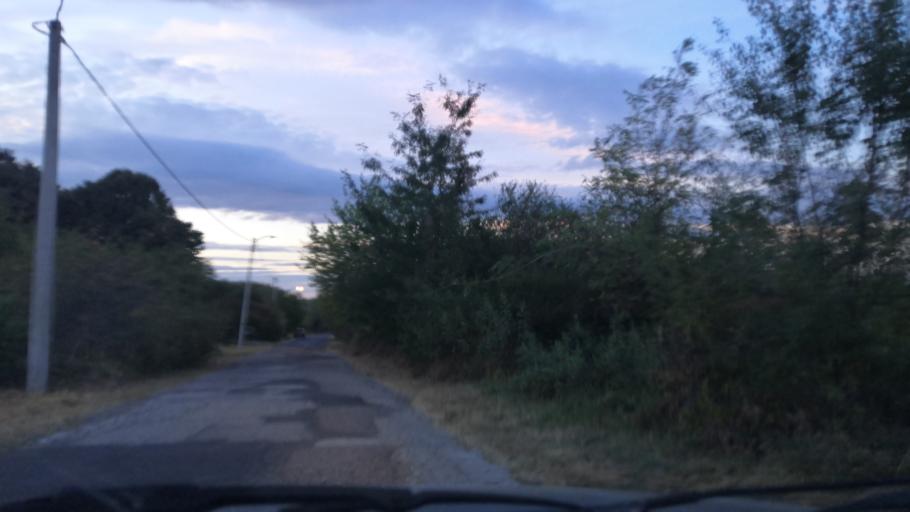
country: RO
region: Mehedinti
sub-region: Comuna Gogosu
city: Balta Verde
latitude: 44.3094
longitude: 22.5489
